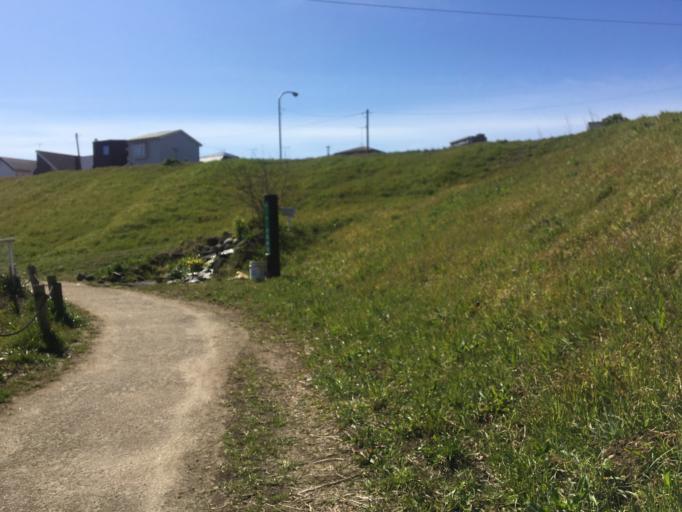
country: JP
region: Saitama
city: Asaka
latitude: 35.8122
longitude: 139.6083
